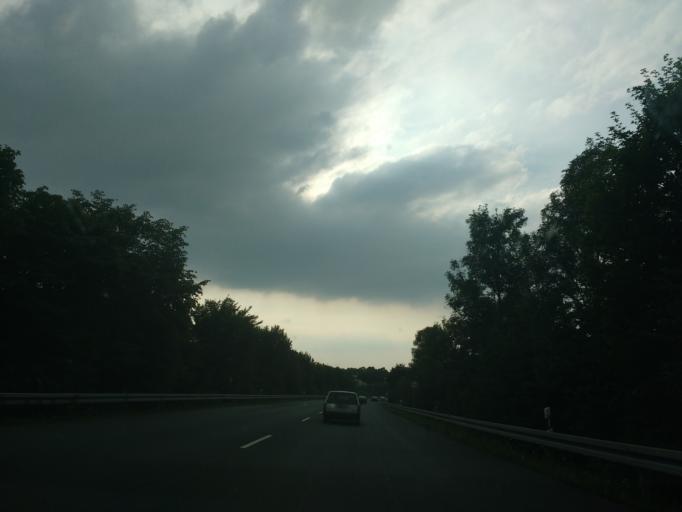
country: DE
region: North Rhine-Westphalia
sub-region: Regierungsbezirk Detmold
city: Paderborn
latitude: 51.6894
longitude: 8.7968
